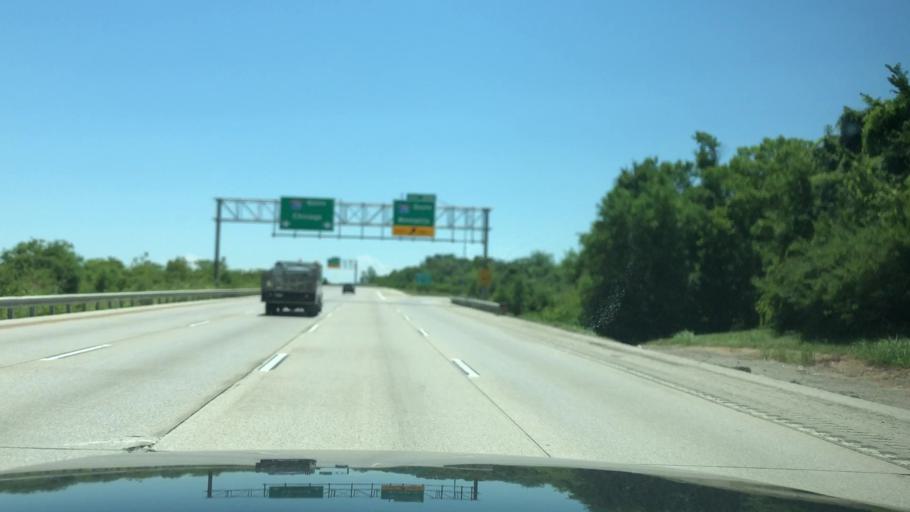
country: US
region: Missouri
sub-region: Saint Louis County
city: Bridgeton
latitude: 38.7724
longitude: -90.4098
